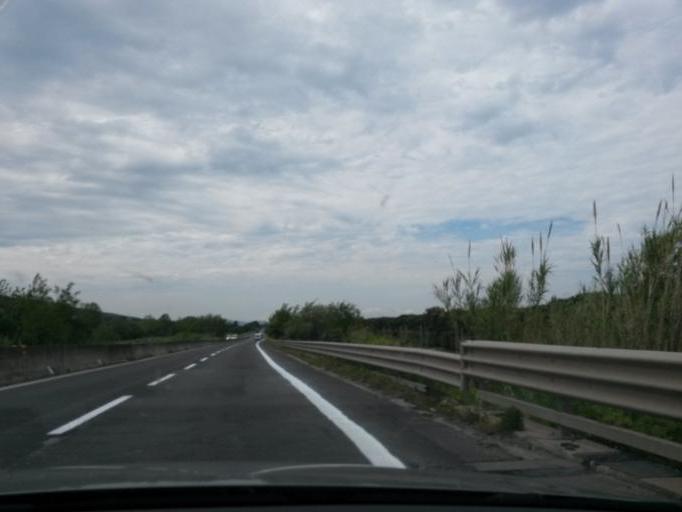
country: IT
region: Tuscany
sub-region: Provincia di Livorno
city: Donoratico
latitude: 43.1492
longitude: 10.5552
